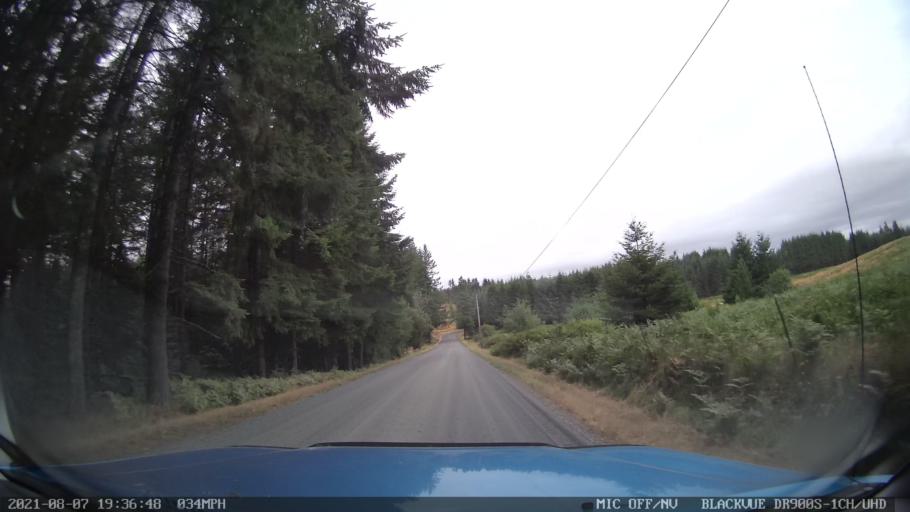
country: US
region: Oregon
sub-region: Marion County
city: Silverton
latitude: 44.9362
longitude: -122.6567
